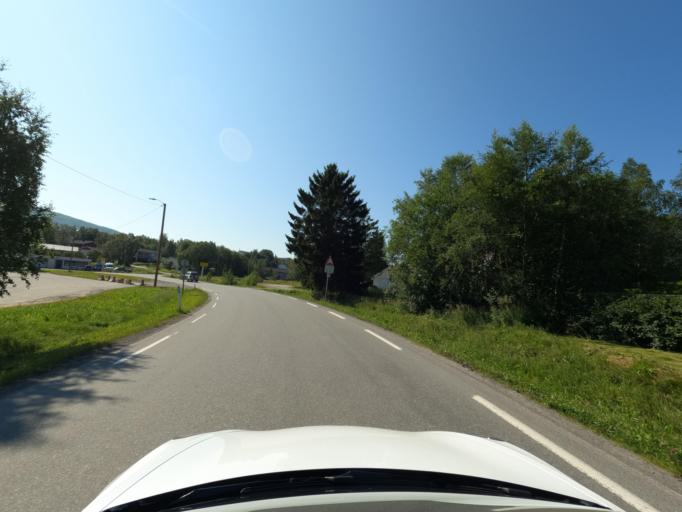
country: NO
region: Nordland
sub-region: Ballangen
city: Ballangen
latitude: 68.3435
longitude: 16.8274
